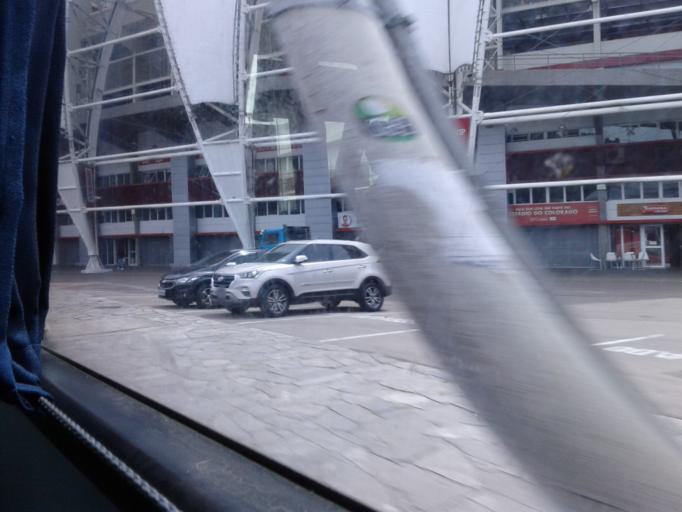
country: BR
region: Rio Grande do Sul
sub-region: Porto Alegre
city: Porto Alegre
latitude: -30.0656
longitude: -51.2342
